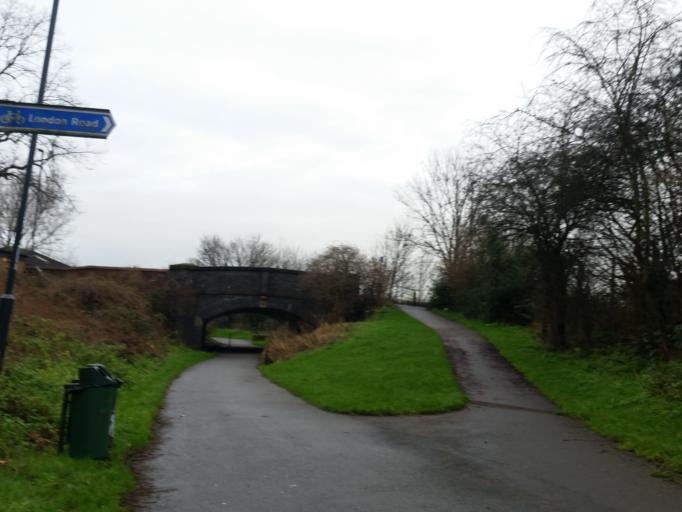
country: GB
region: England
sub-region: Derby
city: Derby
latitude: 52.9037
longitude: -1.4458
